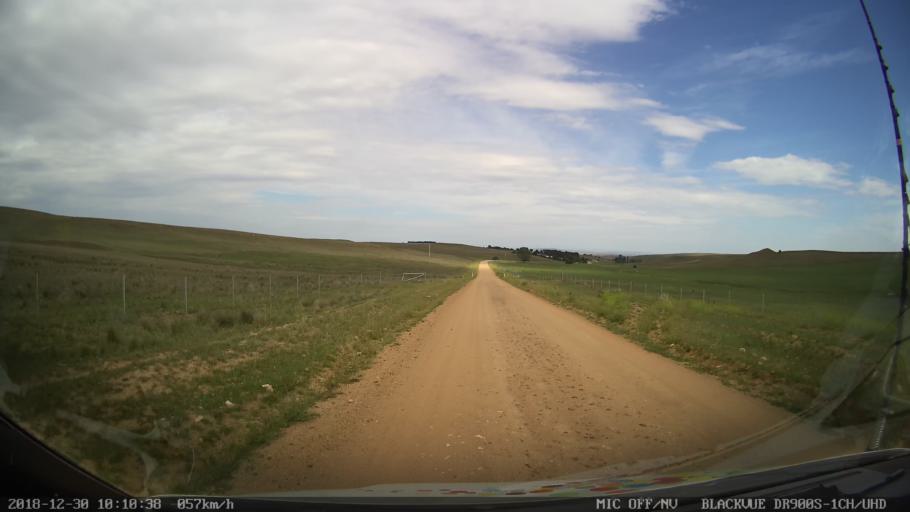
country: AU
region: New South Wales
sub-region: Cooma-Monaro
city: Cooma
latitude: -36.5503
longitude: 149.0930
